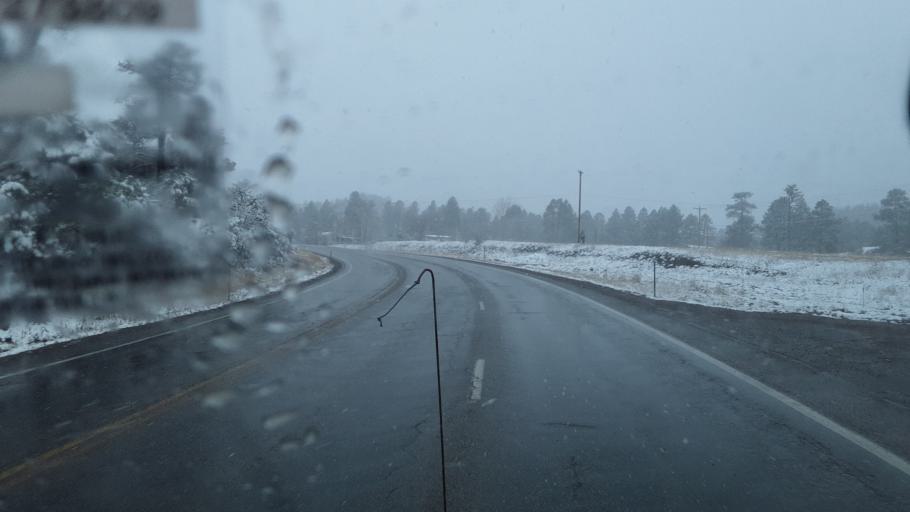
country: US
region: Colorado
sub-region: Archuleta County
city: Pagosa Springs
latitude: 37.2733
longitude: -107.0351
